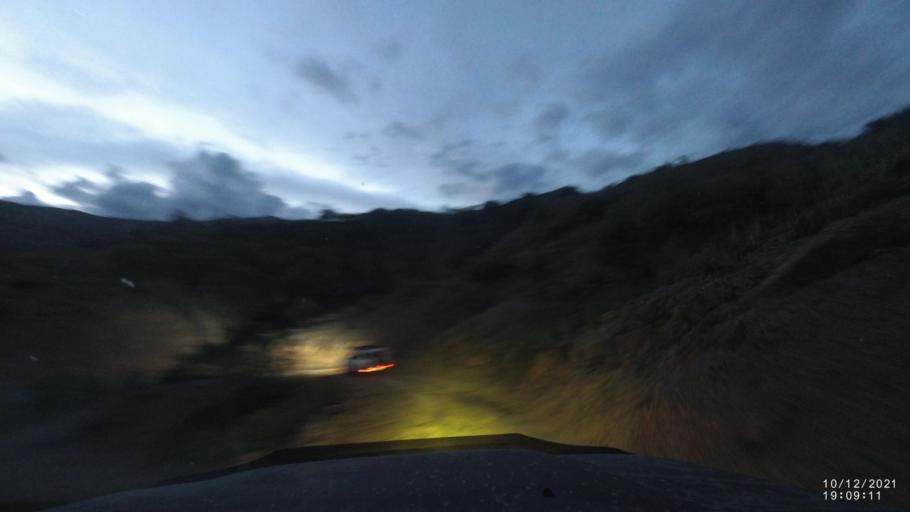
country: BO
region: Cochabamba
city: Tarata
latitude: -17.9114
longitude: -65.9383
